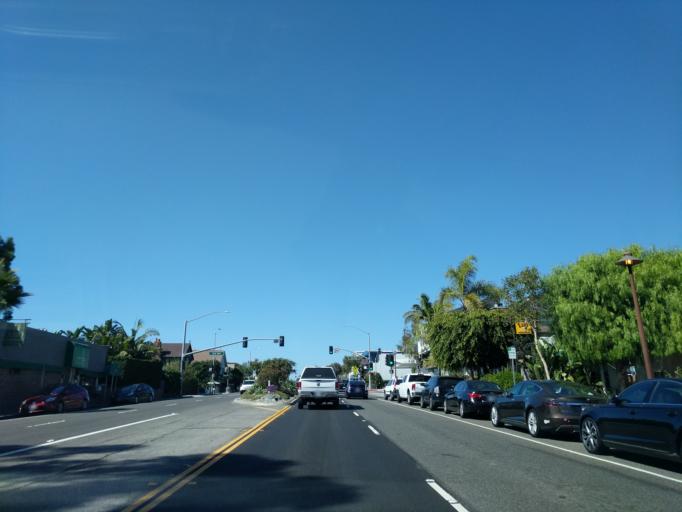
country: US
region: California
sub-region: Orange County
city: Laguna Niguel
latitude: 33.5016
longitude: -117.7437
